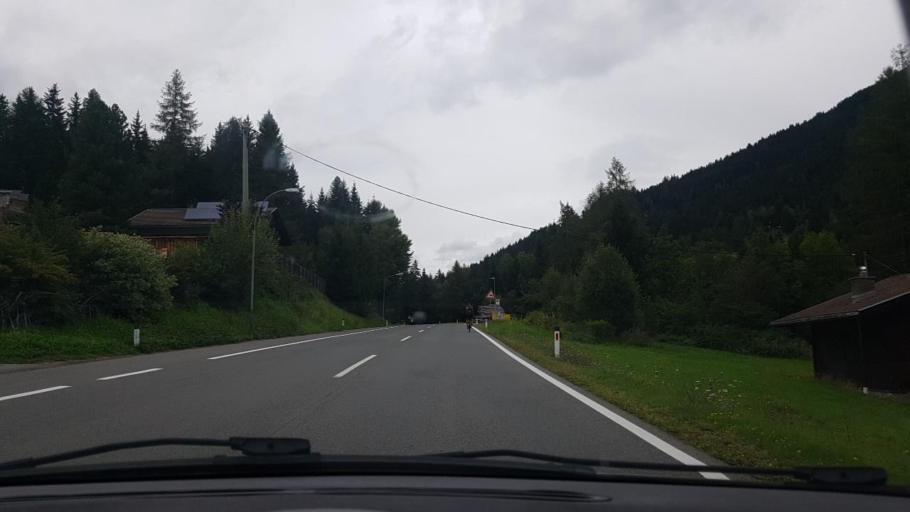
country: AT
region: Tyrol
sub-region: Politischer Bezirk Lienz
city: Dolsach
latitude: 46.8417
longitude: 12.8502
